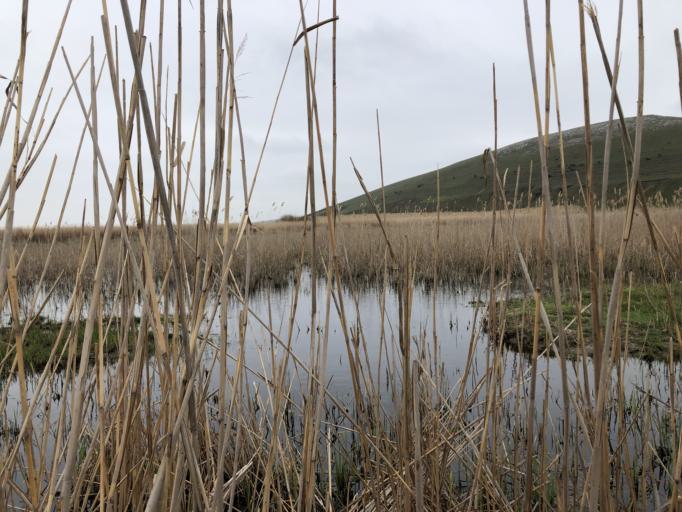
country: RO
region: Tulcea
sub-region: Comuna Sarichioi
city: Enisala
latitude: 44.8849
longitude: 28.8406
